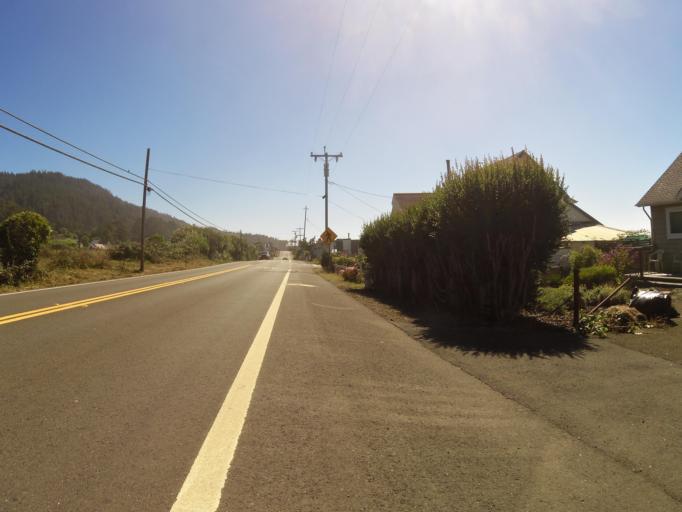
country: US
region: California
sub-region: Mendocino County
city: Fort Bragg
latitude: 39.6401
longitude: -123.7849
